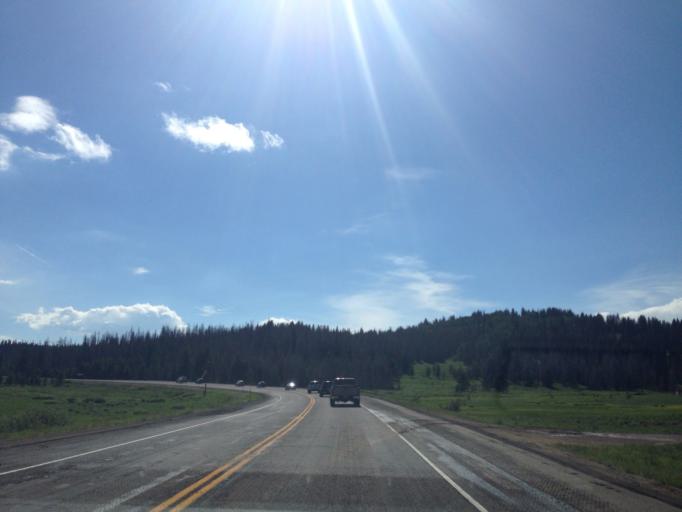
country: US
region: Colorado
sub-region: Routt County
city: Steamboat Springs
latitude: 40.3758
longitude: -106.7322
